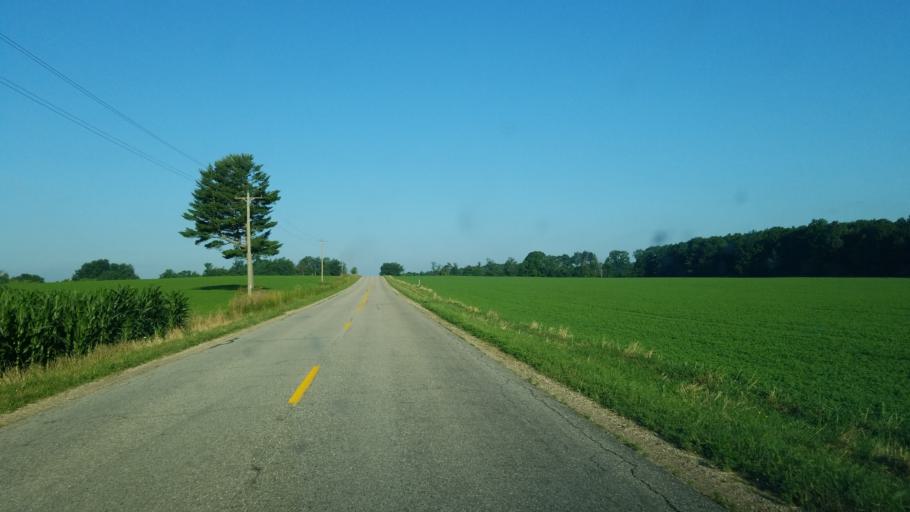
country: US
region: Michigan
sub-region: Montcalm County
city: Lakeview
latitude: 43.5169
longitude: -85.1489
